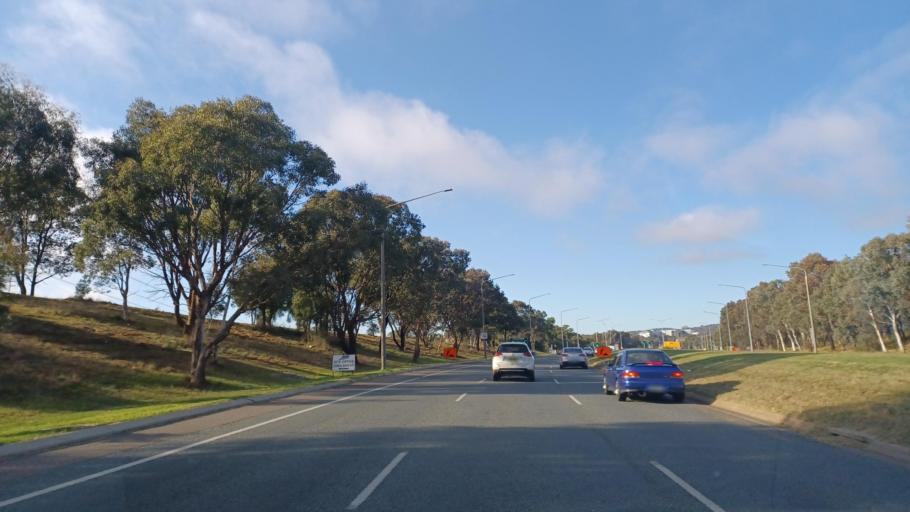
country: AU
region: Australian Capital Territory
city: Belconnen
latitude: -35.2237
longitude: 149.0728
